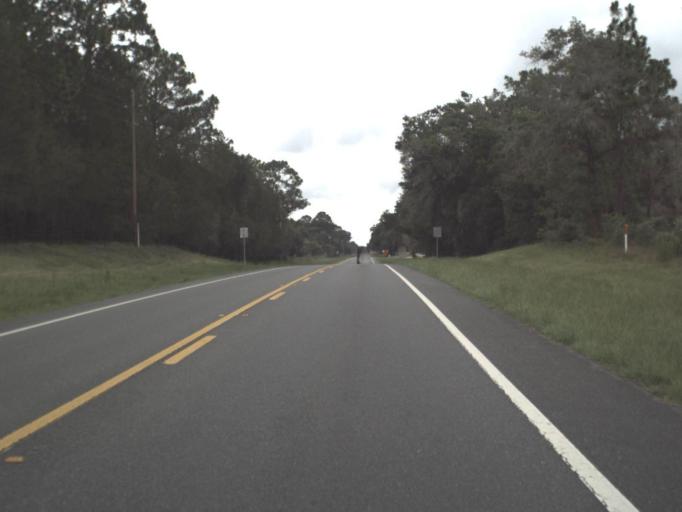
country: US
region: Florida
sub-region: Levy County
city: Williston
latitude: 29.2915
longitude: -82.4468
